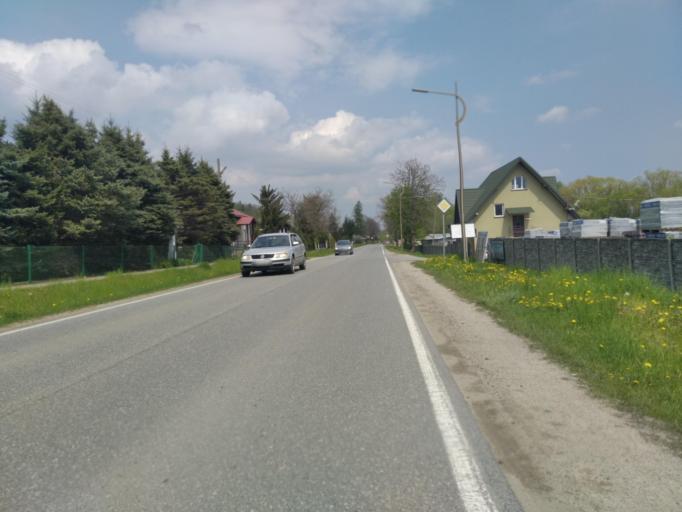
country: PL
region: Subcarpathian Voivodeship
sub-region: Powiat krosnienski
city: Rymanow
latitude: 49.5657
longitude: 21.8622
